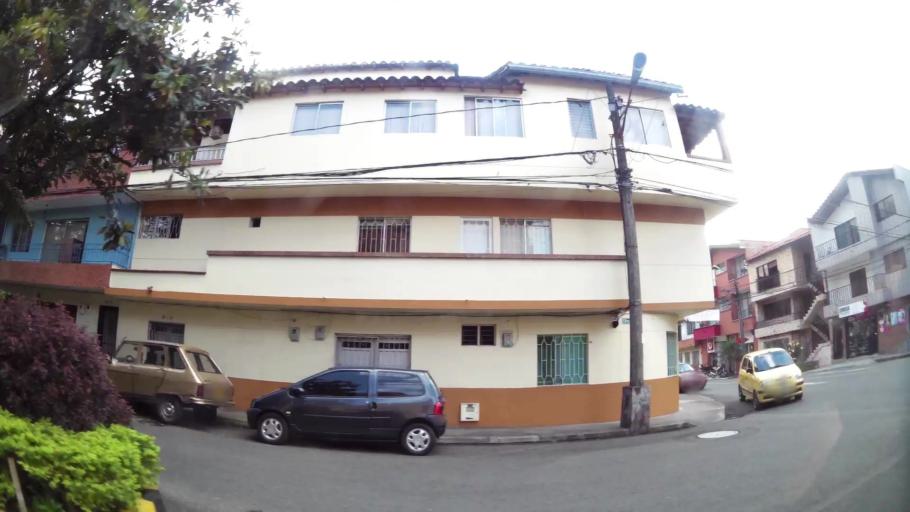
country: CO
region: Antioquia
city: Envigado
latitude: 6.1757
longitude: -75.5818
